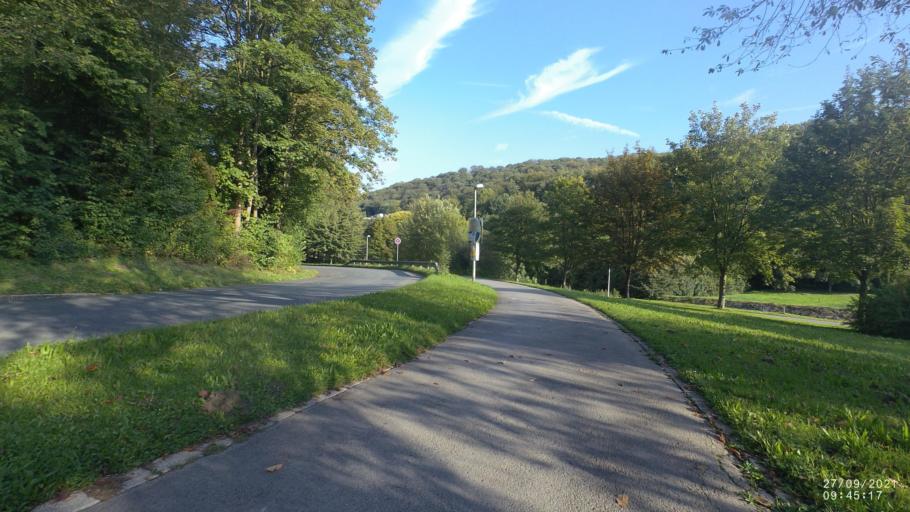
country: DE
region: North Rhine-Westphalia
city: Iserlohn
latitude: 51.3891
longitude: 7.7117
